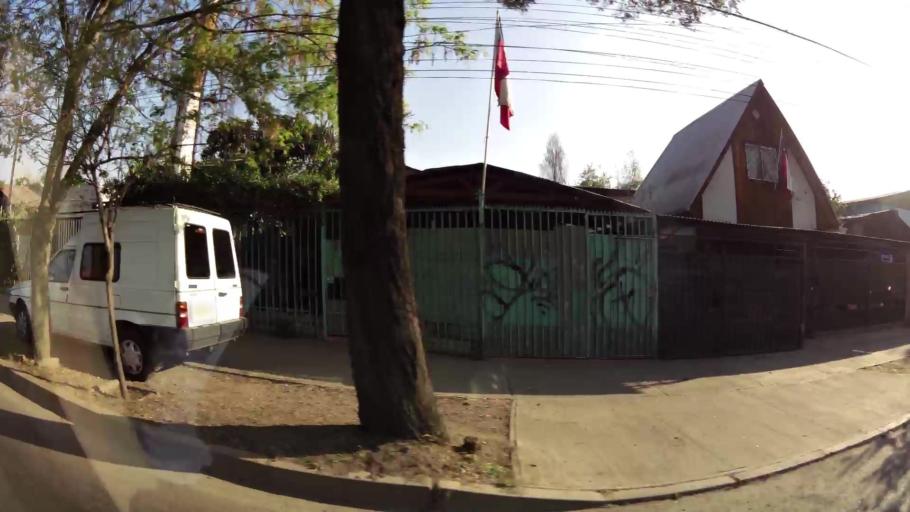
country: CL
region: Santiago Metropolitan
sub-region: Provincia de Santiago
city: Santiago
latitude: -33.3845
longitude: -70.6392
